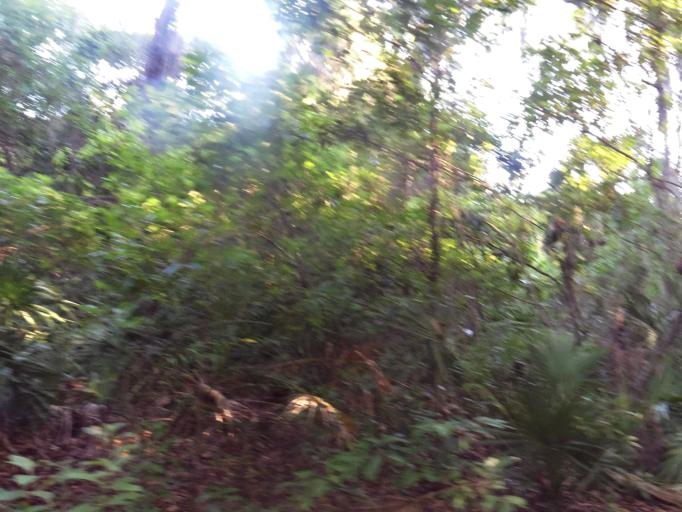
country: US
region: Florida
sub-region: Duval County
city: Atlantic Beach
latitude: 30.3838
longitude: -81.4906
